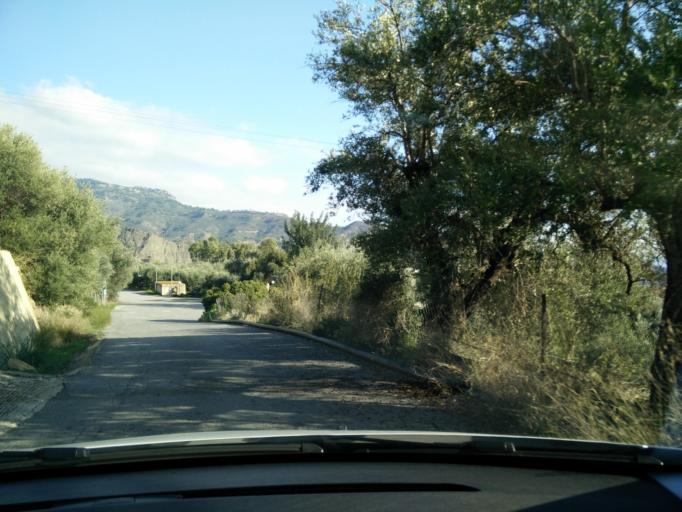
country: GR
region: Crete
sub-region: Nomos Lasithiou
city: Gra Liyia
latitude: 35.0381
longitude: 25.5725
